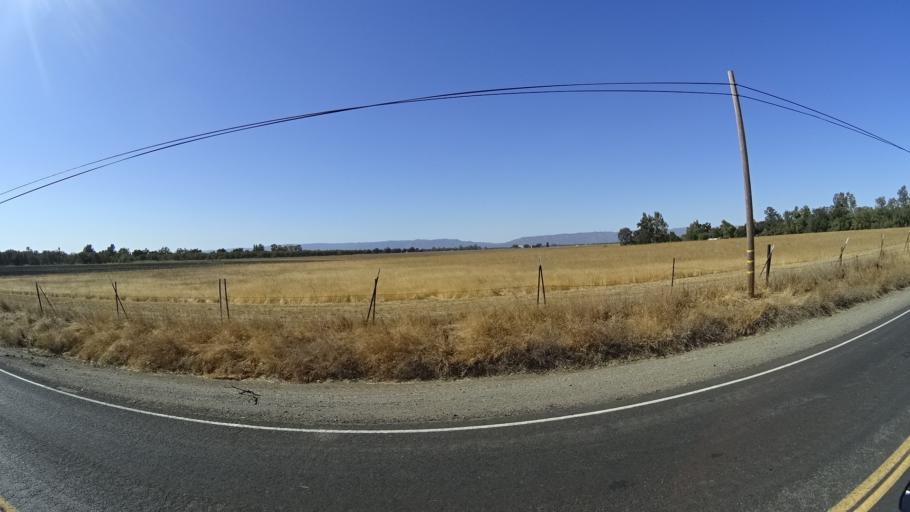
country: US
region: California
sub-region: Solano County
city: Dixon
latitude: 38.5442
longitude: -121.8543
